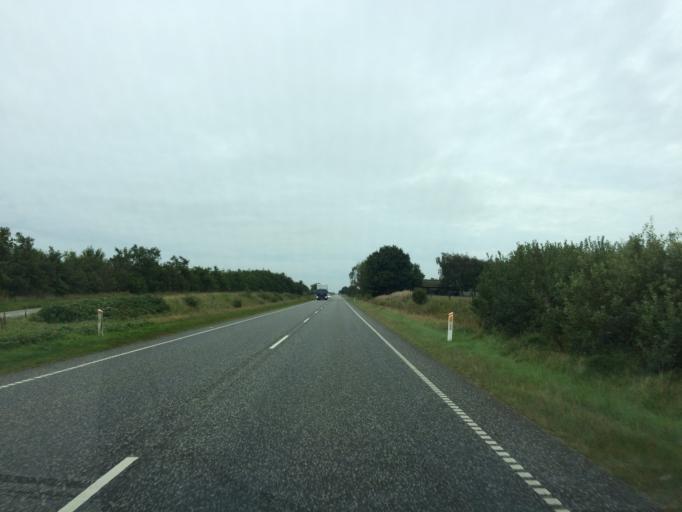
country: DK
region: Central Jutland
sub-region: Herning Kommune
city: Lind
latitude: 56.1029
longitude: 8.9350
